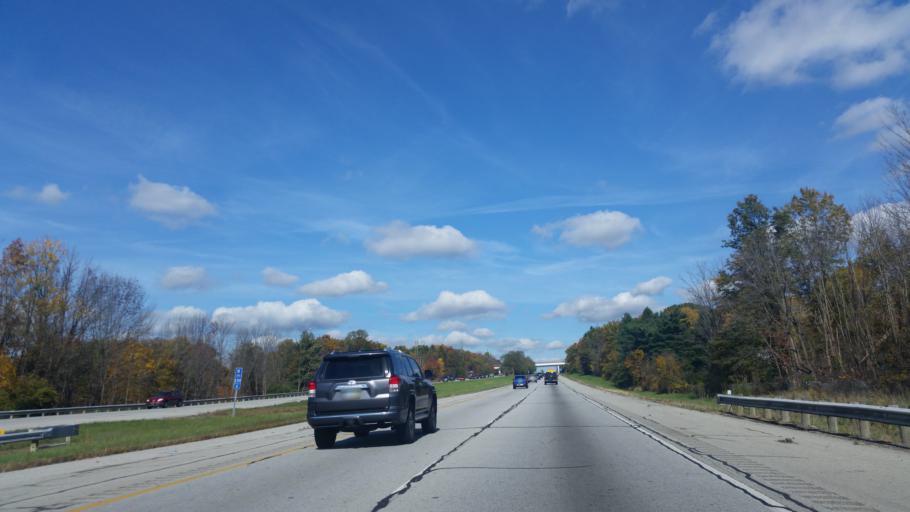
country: US
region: Ohio
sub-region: Summit County
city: Montrose-Ghent
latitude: 41.1696
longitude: -81.6259
